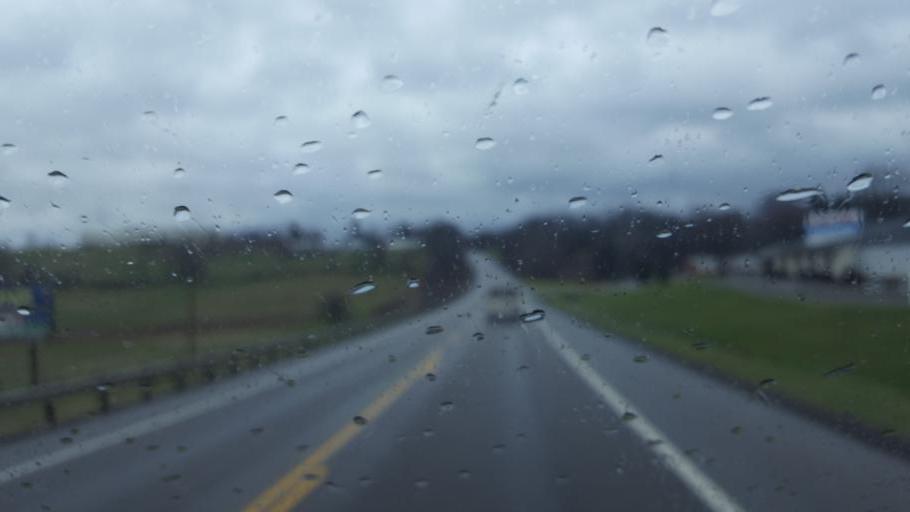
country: US
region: Ohio
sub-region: Holmes County
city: Millersburg
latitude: 40.5535
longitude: -81.8672
